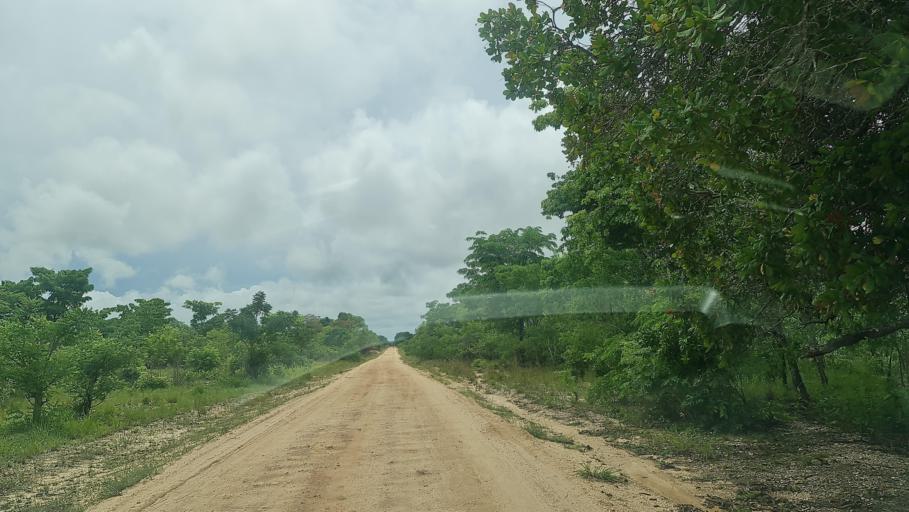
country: MZ
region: Zambezia
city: Quelimane
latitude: -17.2576
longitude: 37.2285
